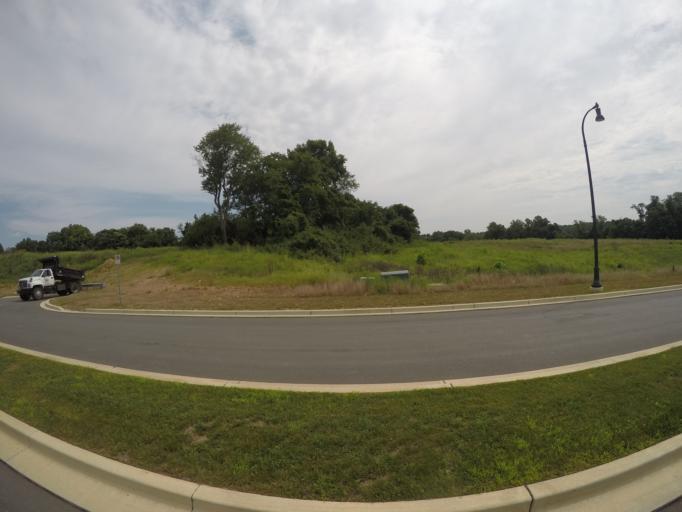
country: US
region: Maryland
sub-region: Montgomery County
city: Clarksburg
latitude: 39.2211
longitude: -77.2849
